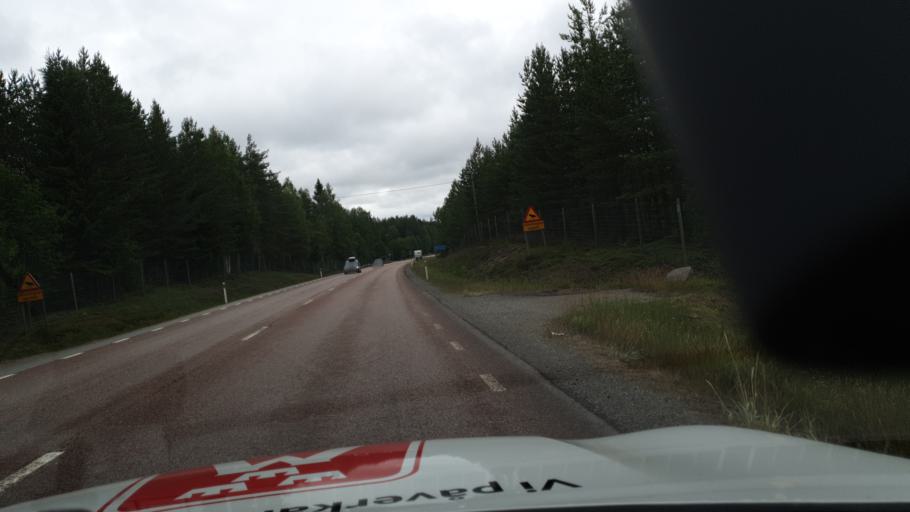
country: SE
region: Vaesterbotten
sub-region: Skelleftea Kommun
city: Burea
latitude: 64.6162
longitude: 21.1796
